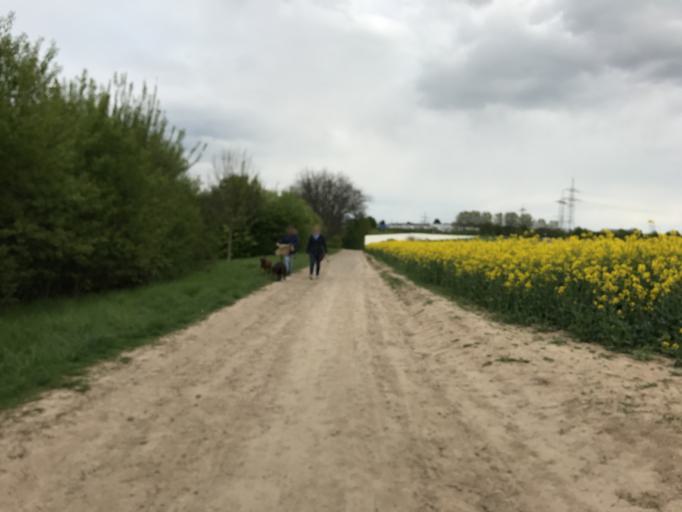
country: DE
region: Rheinland-Pfalz
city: Mainz
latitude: 49.9725
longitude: 8.2580
